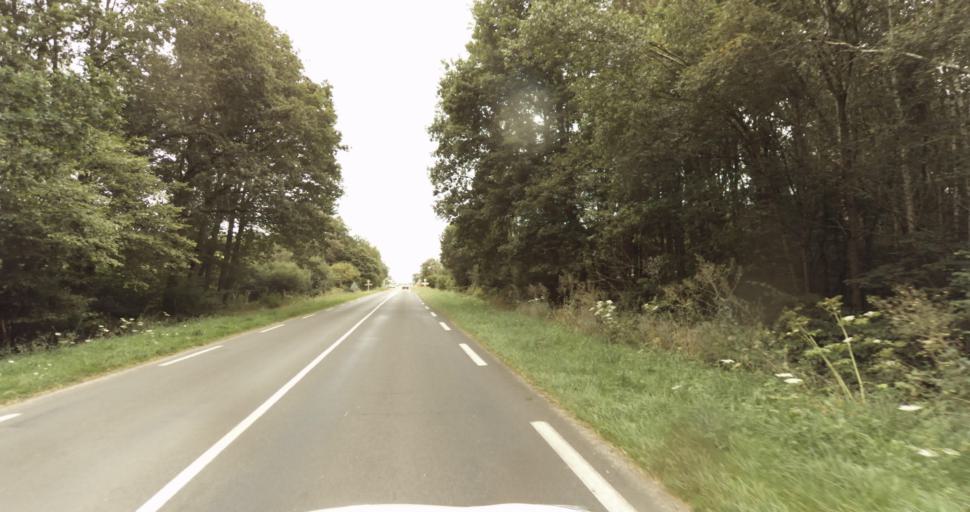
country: FR
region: Haute-Normandie
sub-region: Departement de l'Eure
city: La Madeleine-de-Nonancourt
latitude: 48.8196
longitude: 1.1865
